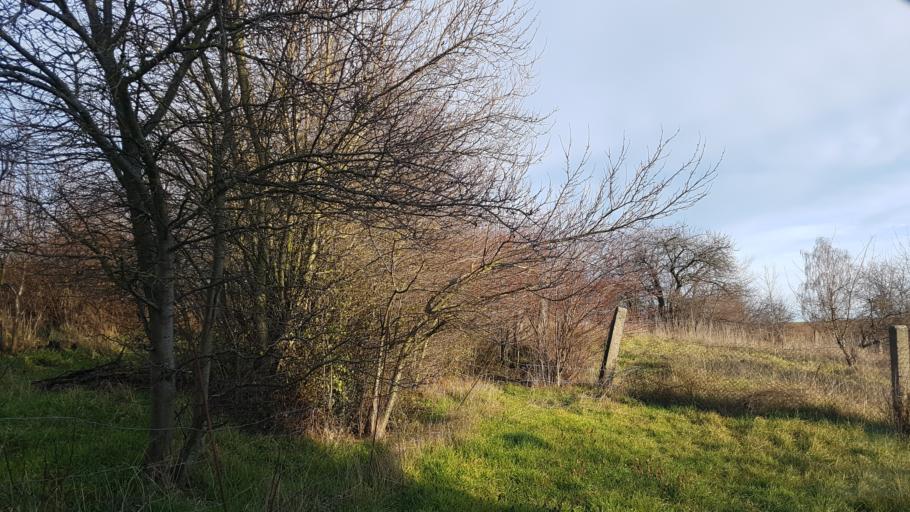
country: DE
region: Saxony
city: Ostrau
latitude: 51.1746
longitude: 13.1712
